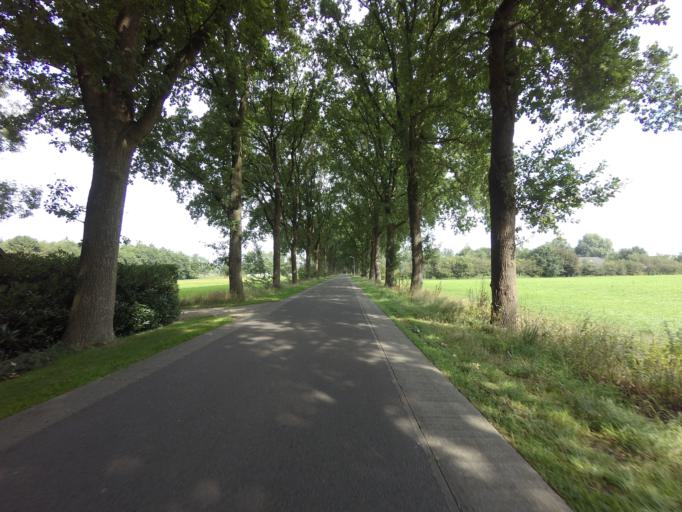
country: NL
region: Overijssel
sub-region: Gemeente Hardenberg
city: Hardenberg
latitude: 52.6782
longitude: 6.5895
